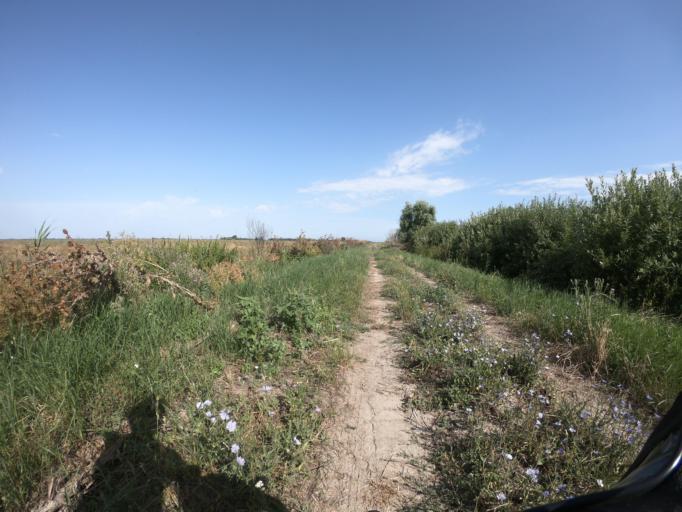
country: HU
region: Hajdu-Bihar
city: Egyek
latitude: 47.5722
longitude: 20.9414
